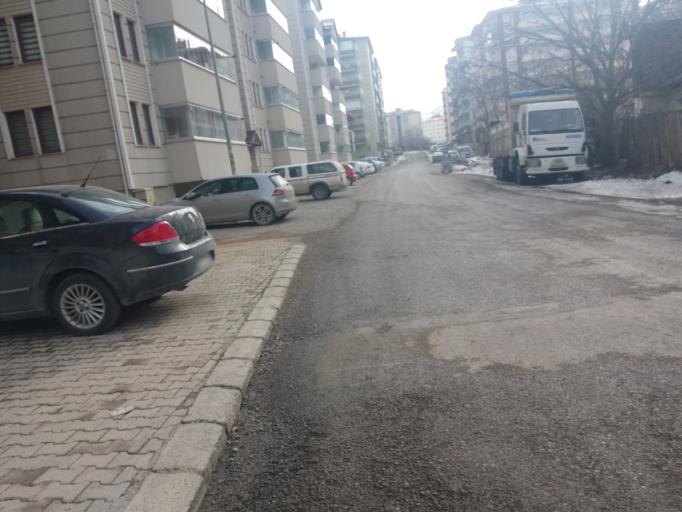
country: TR
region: Gumushane
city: Gumushkhane
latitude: 40.4551
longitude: 39.4900
